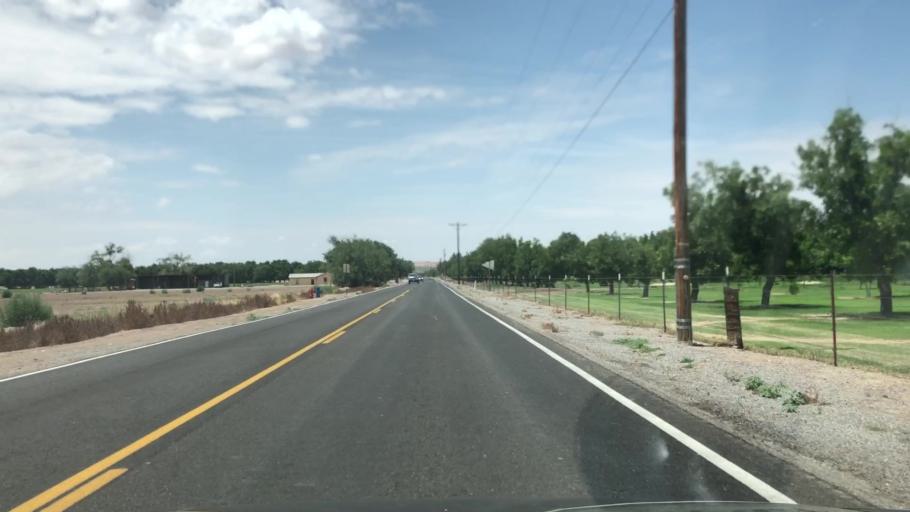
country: US
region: Texas
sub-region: El Paso County
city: Canutillo
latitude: 31.9202
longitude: -106.6351
